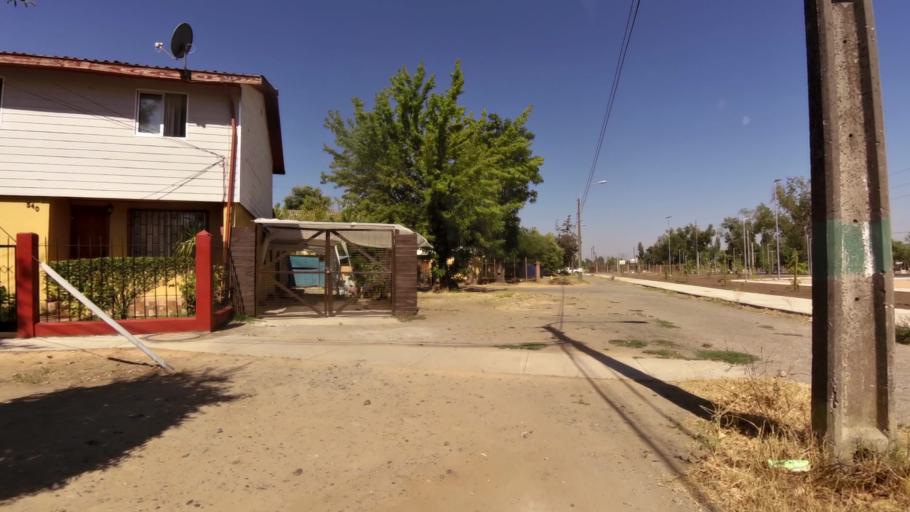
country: CL
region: Maule
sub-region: Provincia de Talca
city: Talca
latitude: -35.4358
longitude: -71.6615
